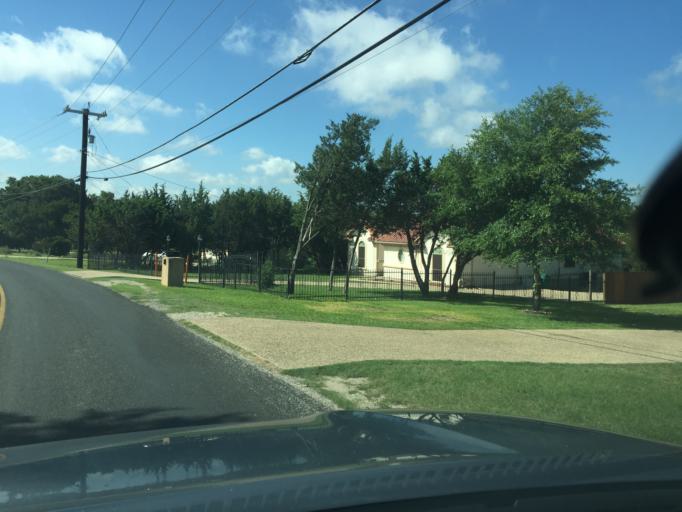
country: US
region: Texas
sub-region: Bexar County
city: Timberwood Park
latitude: 29.7035
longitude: -98.4906
